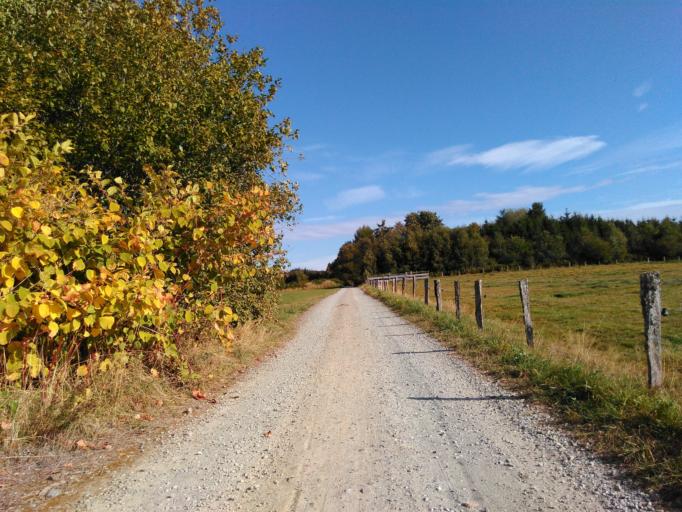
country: BE
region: Wallonia
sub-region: Province du Luxembourg
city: Neufchateau
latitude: 49.9113
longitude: 5.3934
